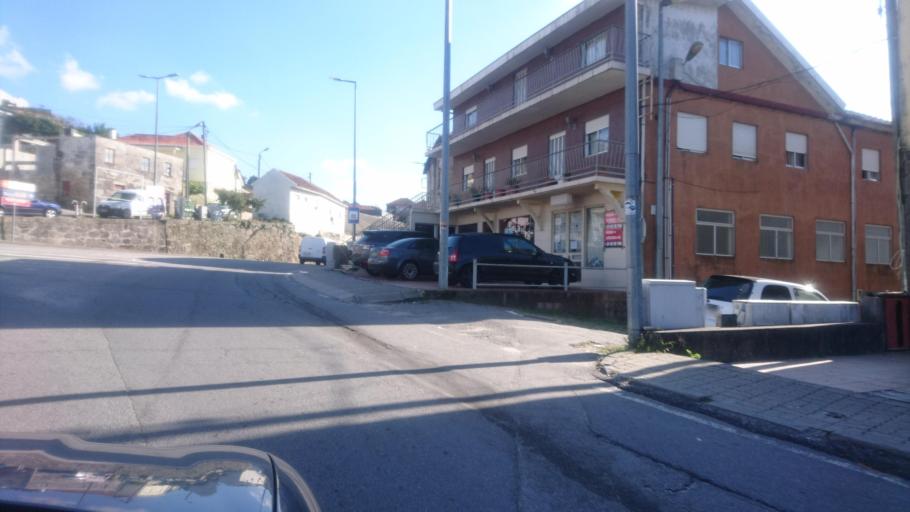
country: PT
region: Porto
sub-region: Paredes
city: Lordelo
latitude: 41.2309
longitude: -8.4072
